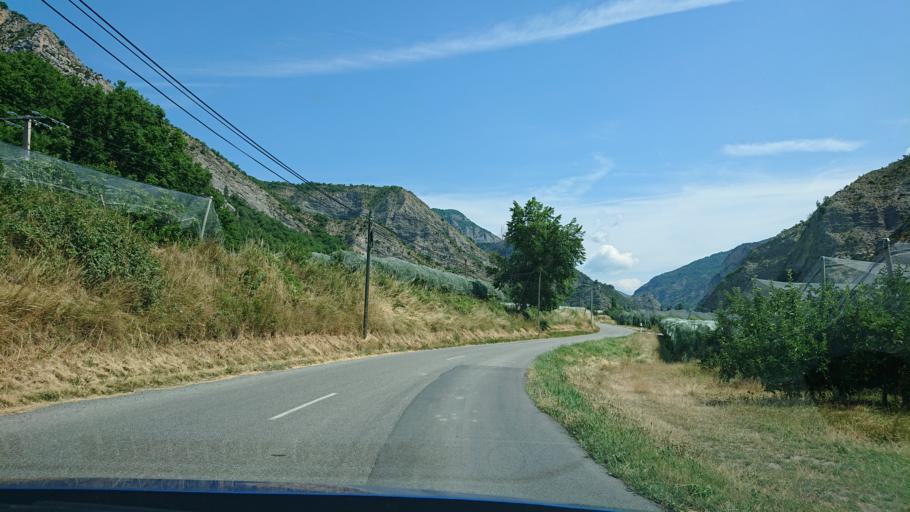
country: FR
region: Provence-Alpes-Cote d'Azur
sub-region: Departement des Hautes-Alpes
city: Tallard
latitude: 44.3619
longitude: 6.0504
